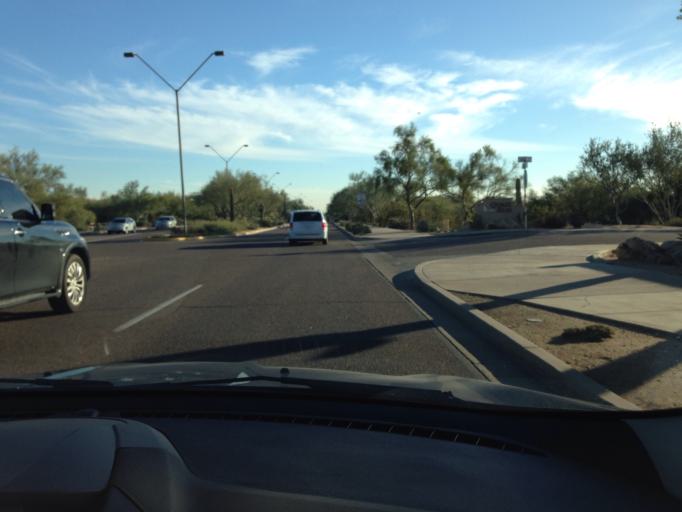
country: US
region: Arizona
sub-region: Maricopa County
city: Cave Creek
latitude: 33.7463
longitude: -111.9783
